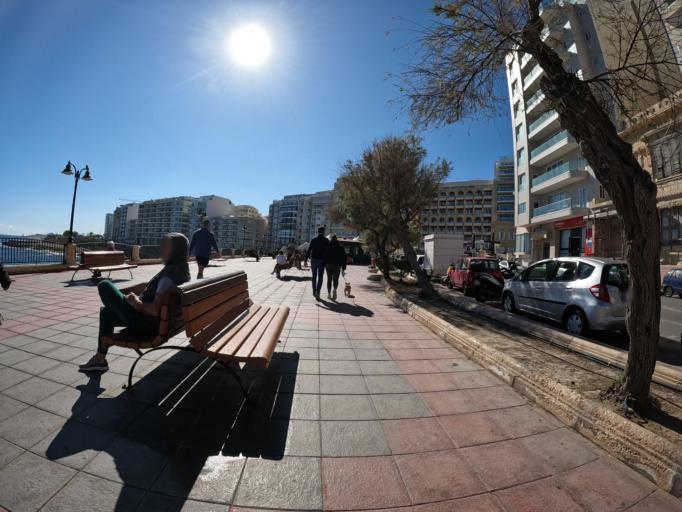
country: MT
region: Tas-Sliema
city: Sliema
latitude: 35.9127
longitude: 14.5068
